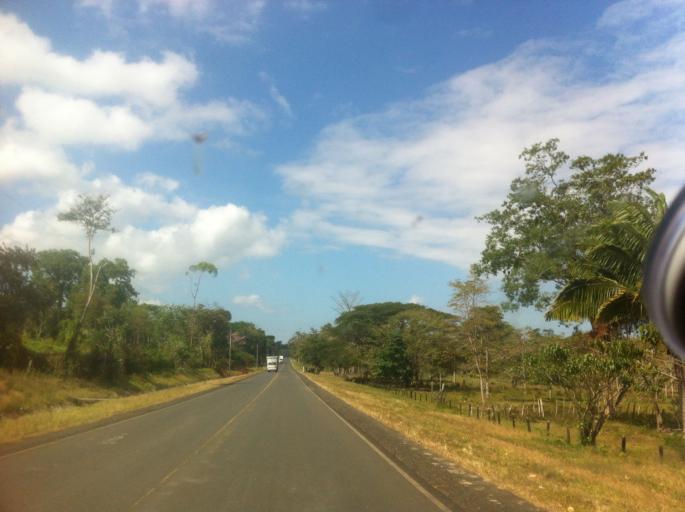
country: NI
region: Rio San Juan
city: San Carlos
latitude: 11.2157
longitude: -84.7109
